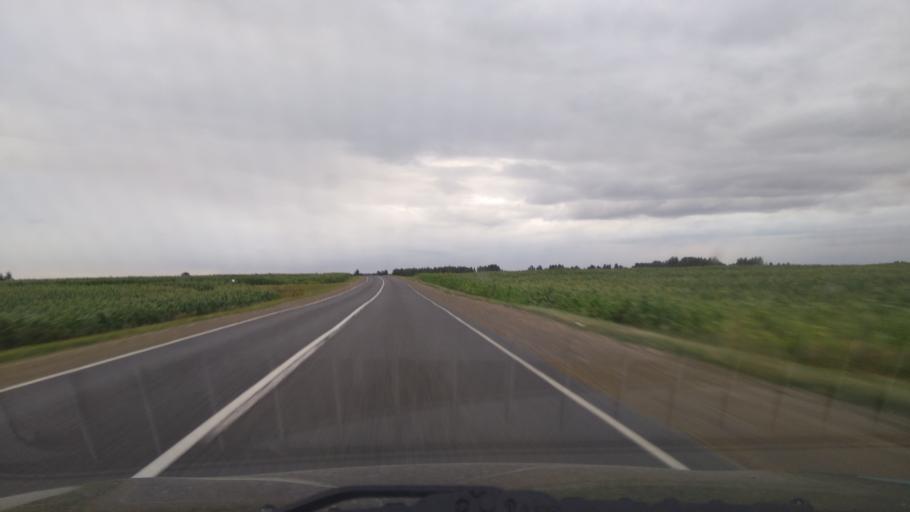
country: BY
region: Brest
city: Byaroza
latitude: 52.4312
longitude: 24.9808
